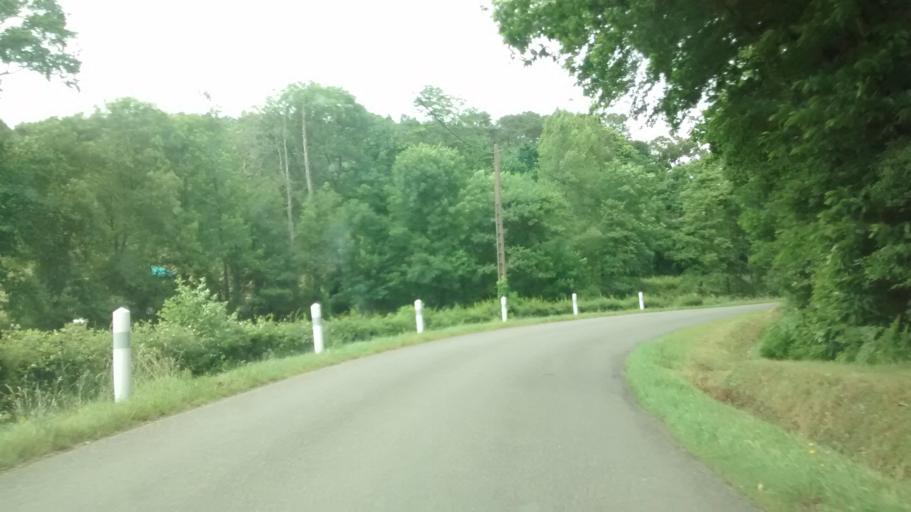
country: FR
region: Brittany
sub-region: Departement du Morbihan
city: Ruffiac
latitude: 47.8421
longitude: -2.2087
